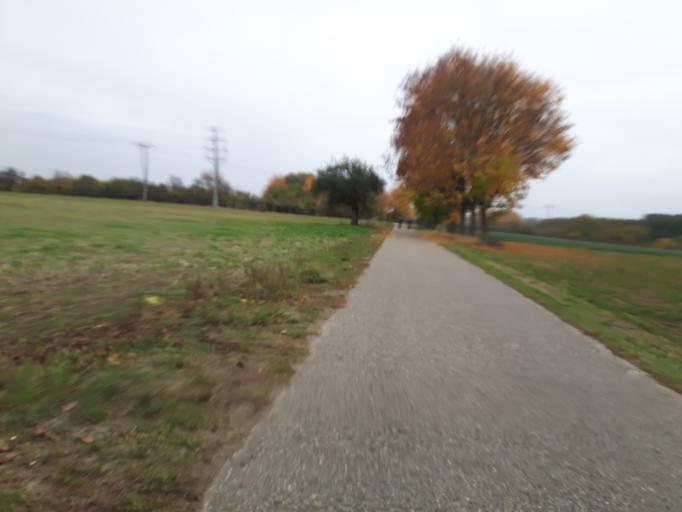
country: DE
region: Baden-Wuerttemberg
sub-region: Karlsruhe Region
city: Malsch
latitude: 49.2181
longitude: 8.6813
